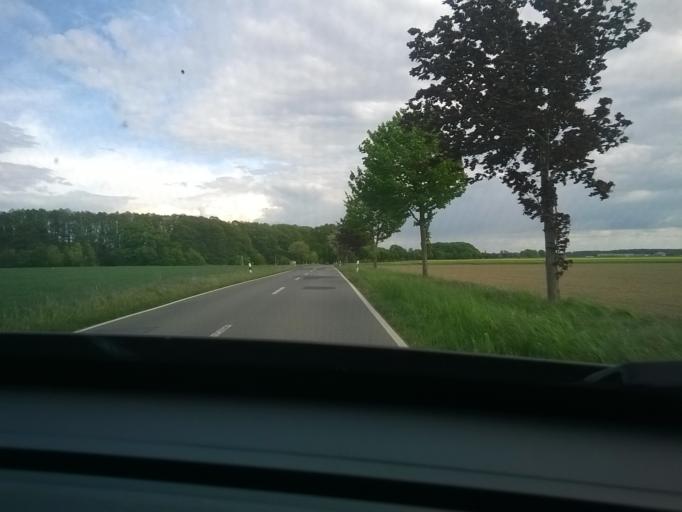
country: DE
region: Brandenburg
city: Wittstock
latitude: 53.1309
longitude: 12.5053
